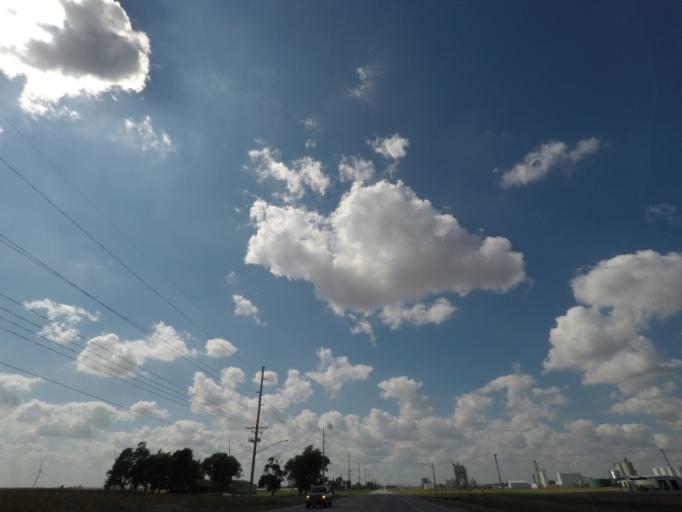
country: US
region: Iowa
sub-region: Story County
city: Nevada
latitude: 42.0231
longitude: -93.5001
